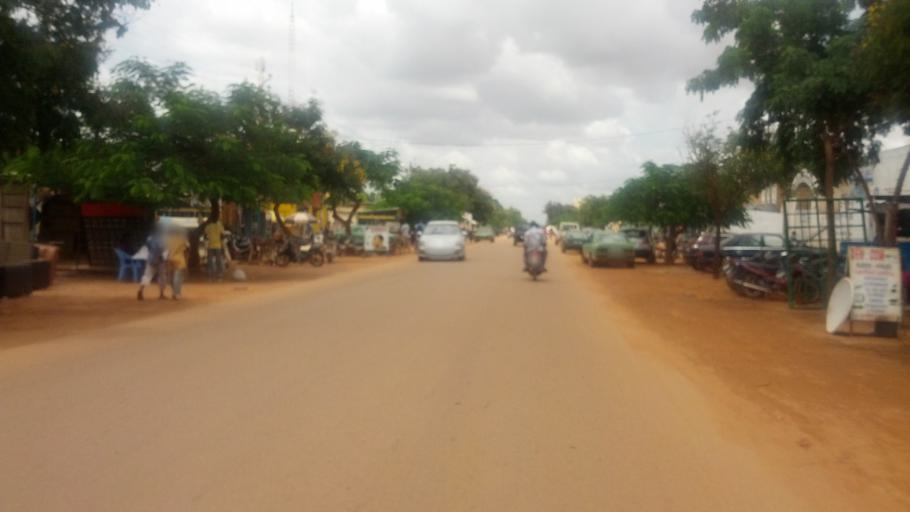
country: BF
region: Centre
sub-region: Kadiogo Province
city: Ouagadougou
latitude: 12.3418
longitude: -1.5067
